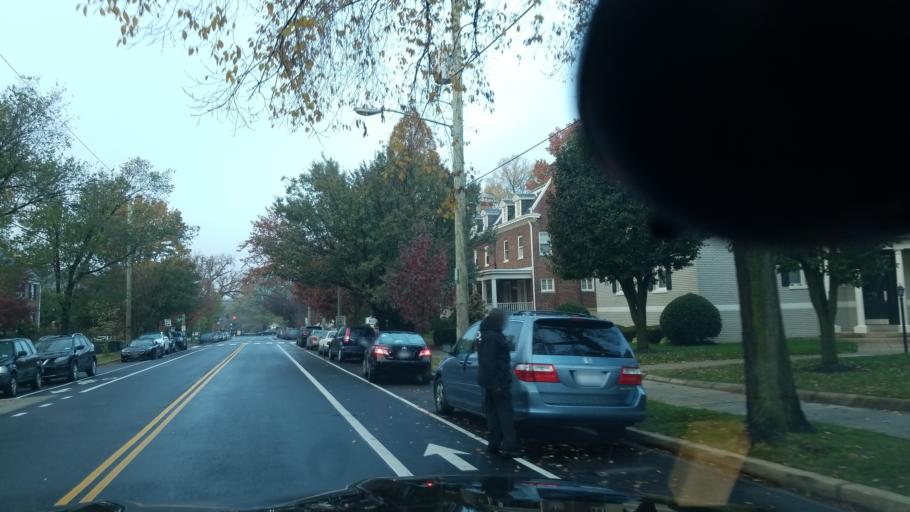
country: US
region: Maryland
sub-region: Montgomery County
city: Silver Spring
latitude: 38.9736
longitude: -77.0251
